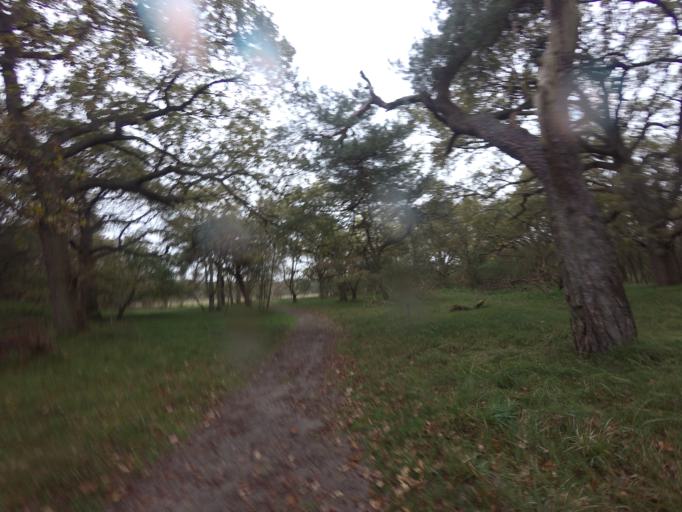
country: NL
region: South Holland
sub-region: Gemeente Leidschendam-Voorburg
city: Voorburg
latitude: 52.1308
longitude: 4.3446
